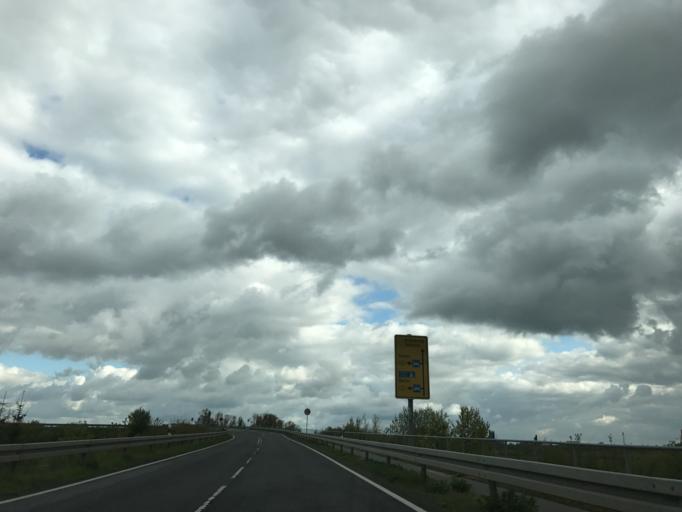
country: DE
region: Brandenburg
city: Wustermark
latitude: 52.5538
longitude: 12.9526
